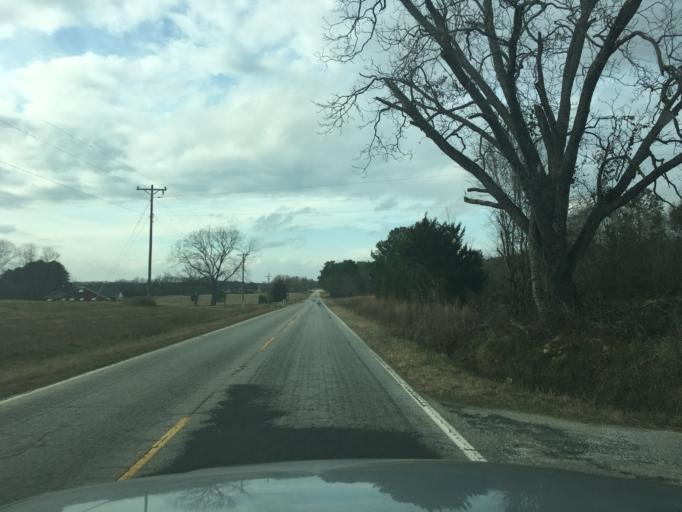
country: US
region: South Carolina
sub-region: Abbeville County
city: Due West
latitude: 34.3302
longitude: -82.4791
